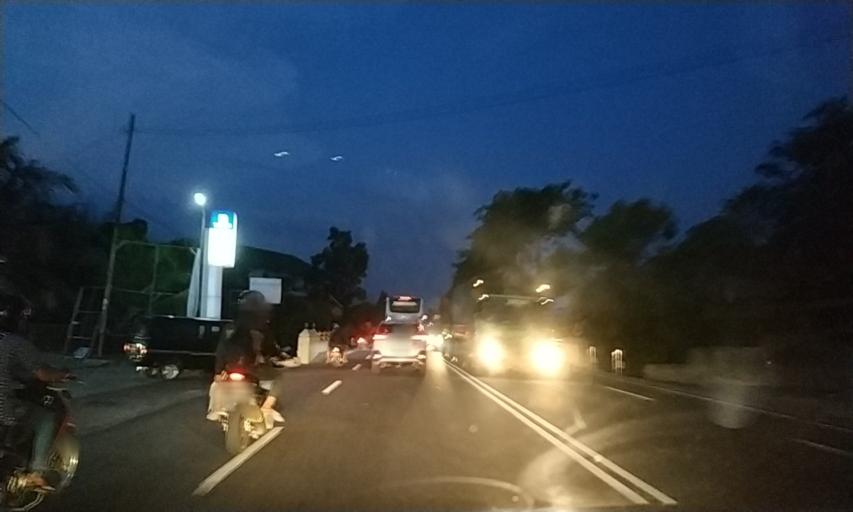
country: ID
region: Daerah Istimewa Yogyakarta
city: Gamping Lor
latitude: -7.8075
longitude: 110.2911
